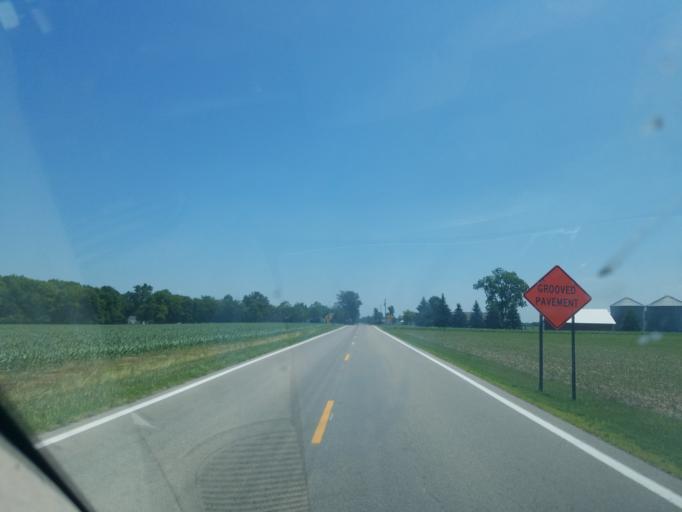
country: US
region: Ohio
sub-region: Allen County
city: Spencerville
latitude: 40.7429
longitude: -84.4210
